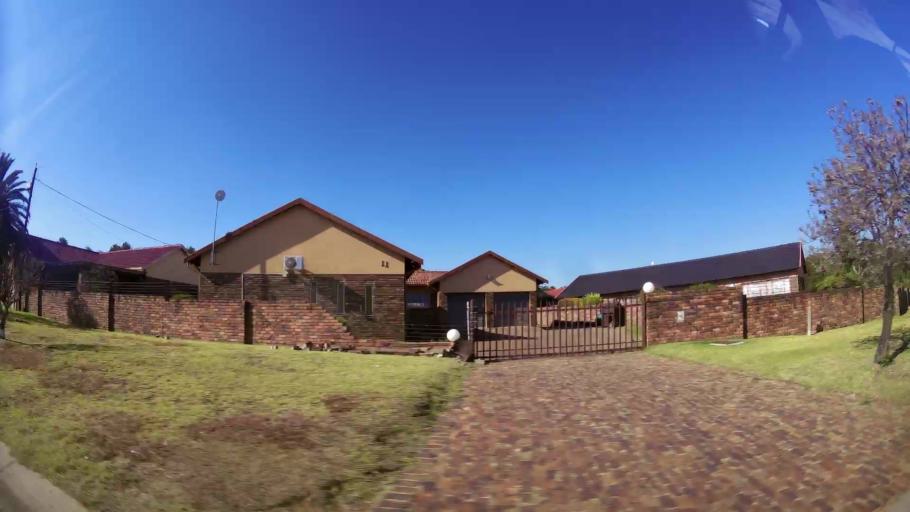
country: ZA
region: Mpumalanga
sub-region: Nkangala District Municipality
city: Witbank
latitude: -25.8875
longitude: 29.2488
